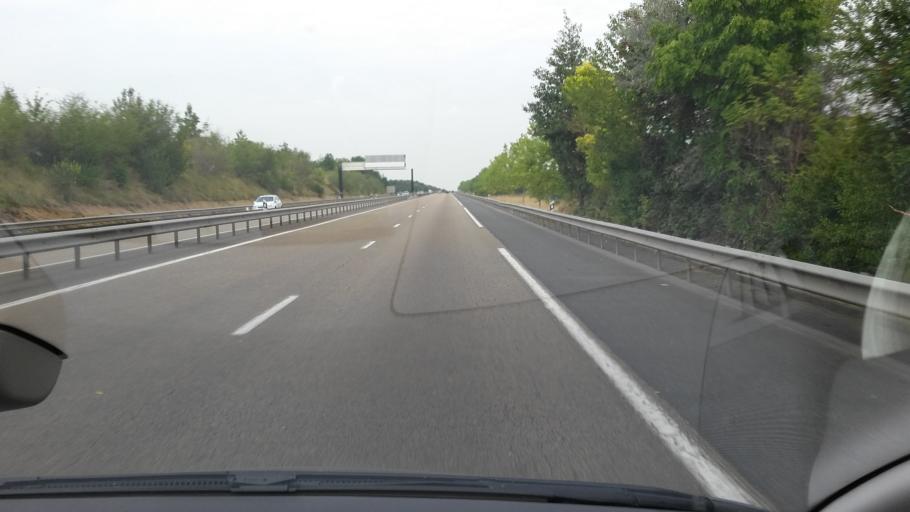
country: FR
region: Champagne-Ardenne
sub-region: Departement de la Marne
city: Witry-les-Reims
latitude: 49.2939
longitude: 4.1297
